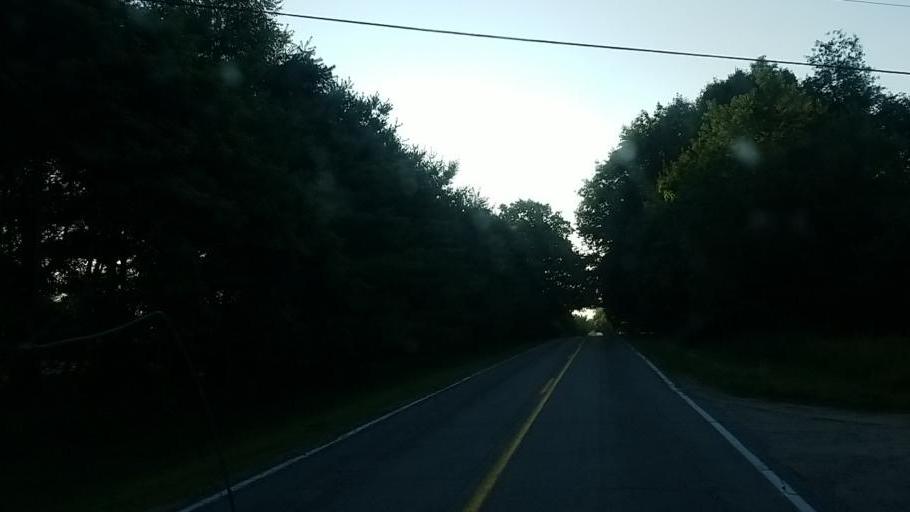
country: US
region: Michigan
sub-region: Montcalm County
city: Lakeview
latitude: 43.3592
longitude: -85.3386
